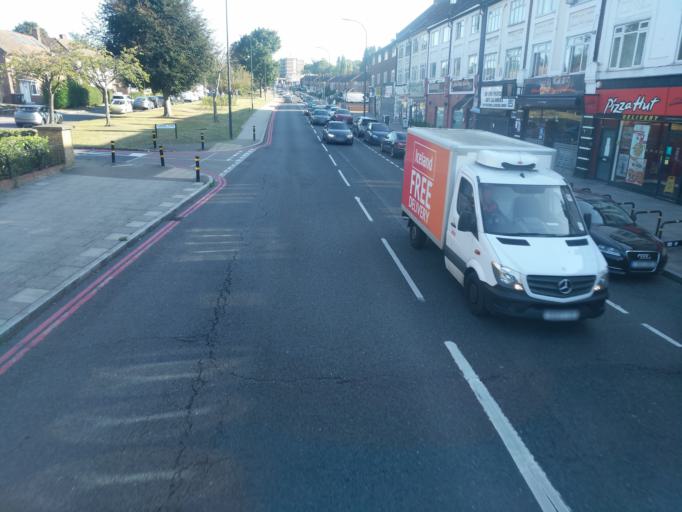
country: GB
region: England
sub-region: Greater London
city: Bromley
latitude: 51.4213
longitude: -0.0016
